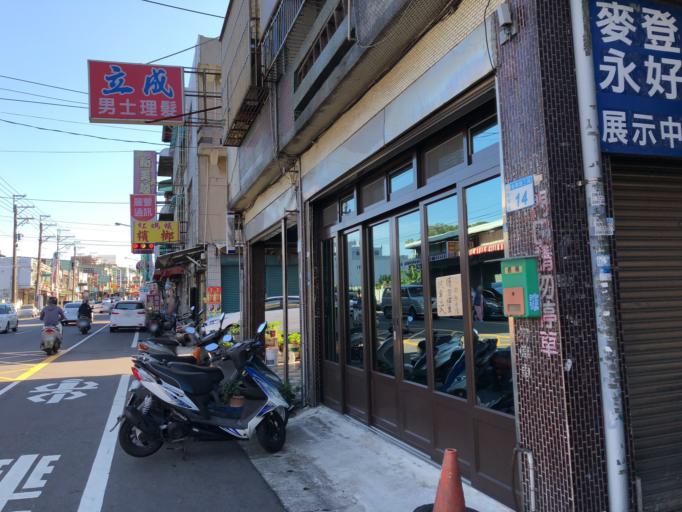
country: TW
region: Taiwan
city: Daxi
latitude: 24.9306
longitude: 121.2267
